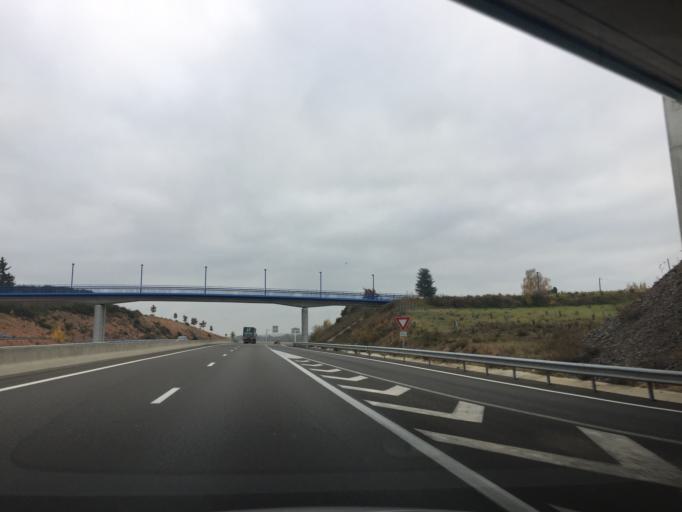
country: FR
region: Auvergne
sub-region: Departement de l'Allier
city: Premilhat
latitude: 46.3340
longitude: 2.5362
